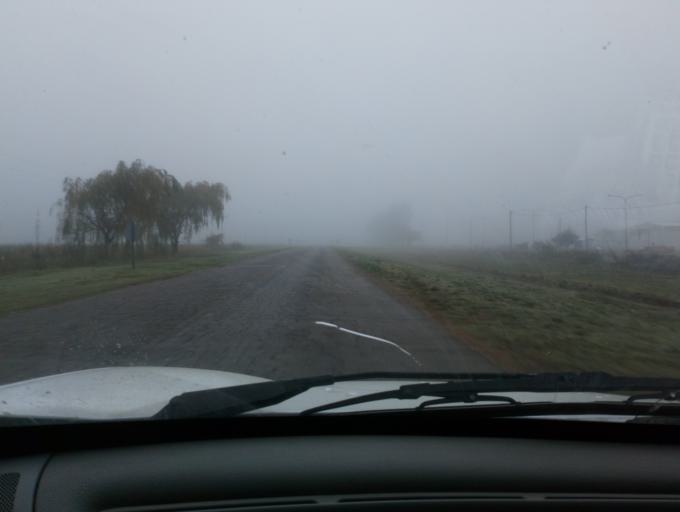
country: AR
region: La Pampa
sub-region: Departamento de Guatrache
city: Guatrache
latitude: -37.6648
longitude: -63.5164
